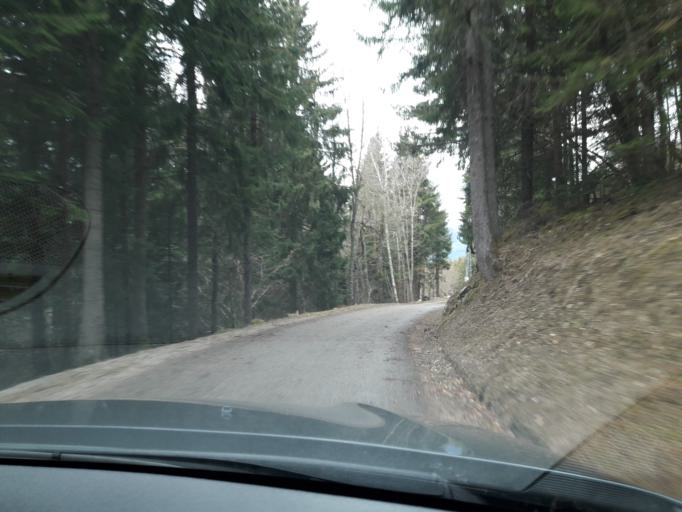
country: FR
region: Rhone-Alpes
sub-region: Departement de l'Isere
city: Le Champ-pres-Froges
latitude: 45.2419
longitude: 5.9805
